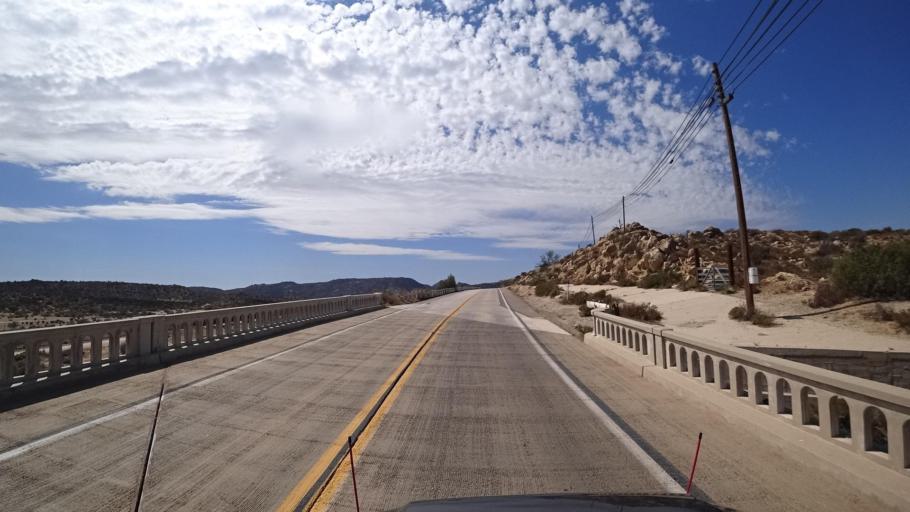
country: MX
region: Baja California
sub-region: Tecate
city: Cereso del Hongo
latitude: 32.6120
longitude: -116.1997
